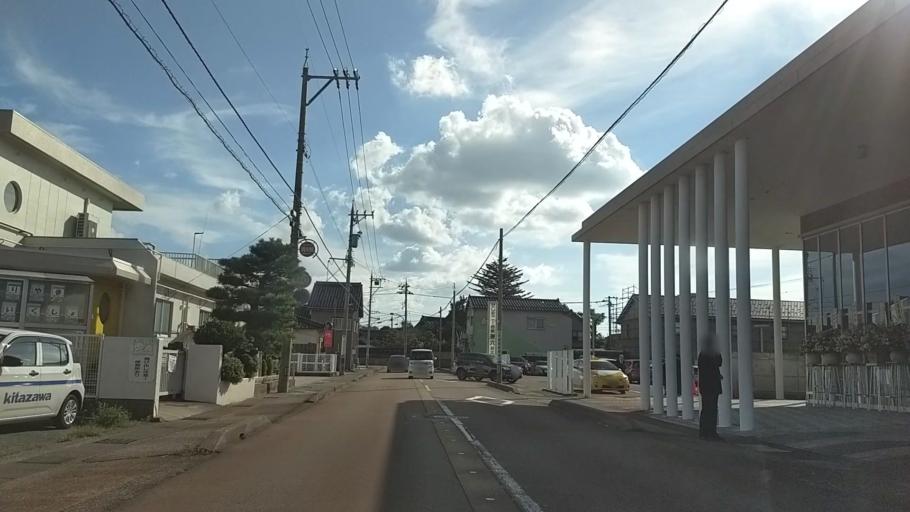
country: JP
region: Ishikawa
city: Kanazawa-shi
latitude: 36.5809
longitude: 136.6668
